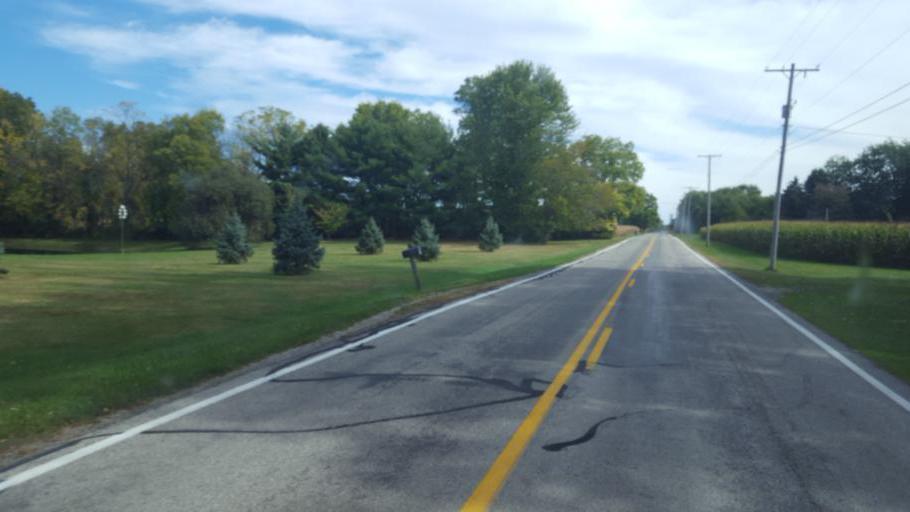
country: US
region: Ohio
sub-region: Erie County
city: Huron
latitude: 41.3649
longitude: -82.5017
